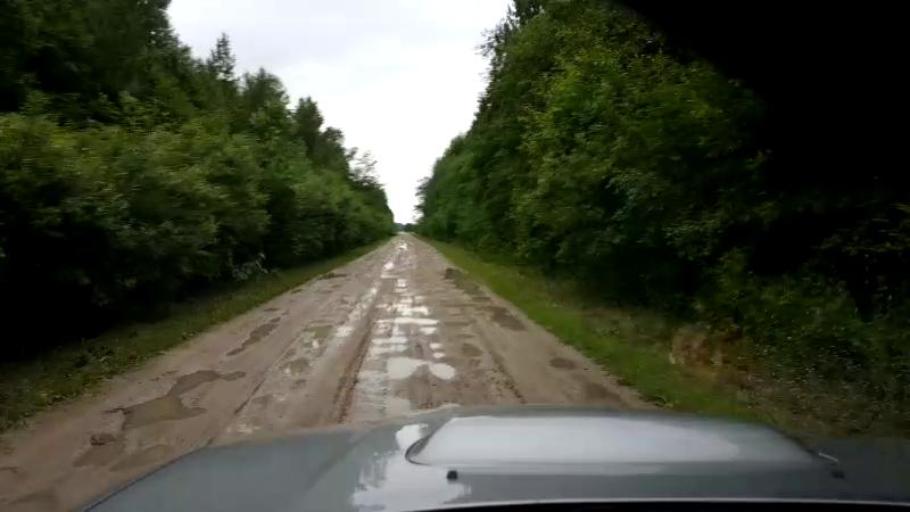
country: EE
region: Paernumaa
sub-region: Halinga vald
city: Parnu-Jaagupi
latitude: 58.5474
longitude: 24.5775
